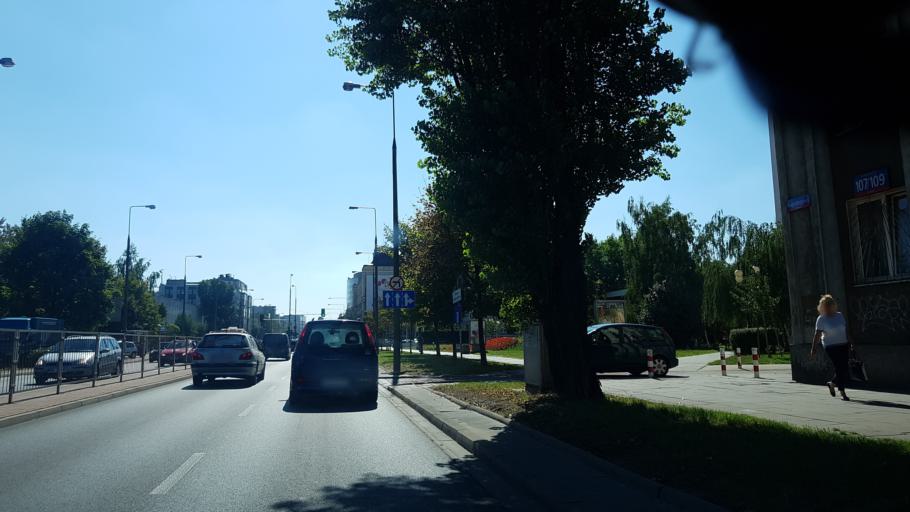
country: PL
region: Masovian Voivodeship
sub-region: Warszawa
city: Mokotow
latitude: 52.1944
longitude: 21.0143
